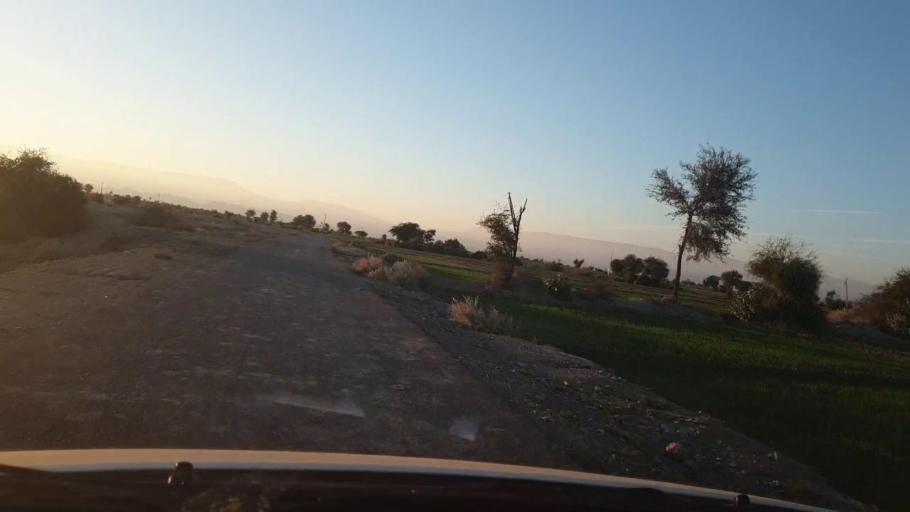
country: PK
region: Sindh
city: Johi
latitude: 26.8292
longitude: 67.4574
